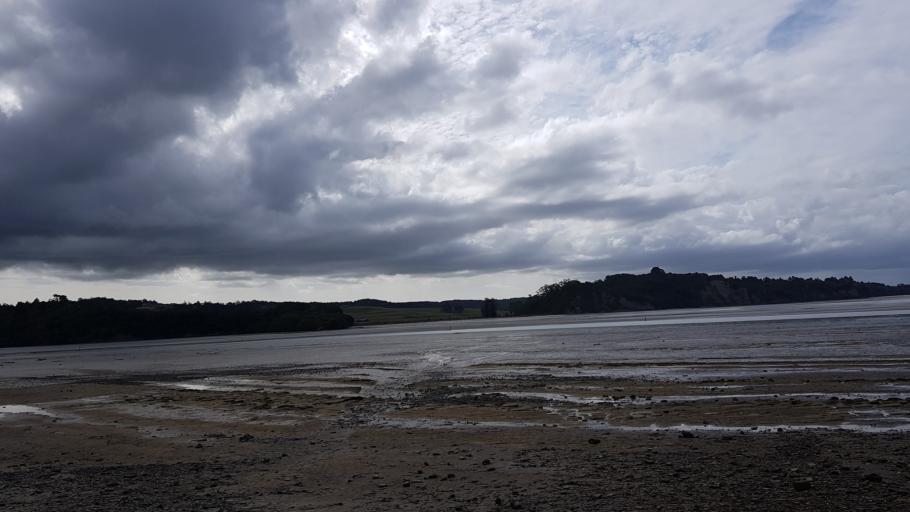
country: NZ
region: Auckland
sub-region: Auckland
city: Rothesay Bay
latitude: -36.6639
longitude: 174.7402
